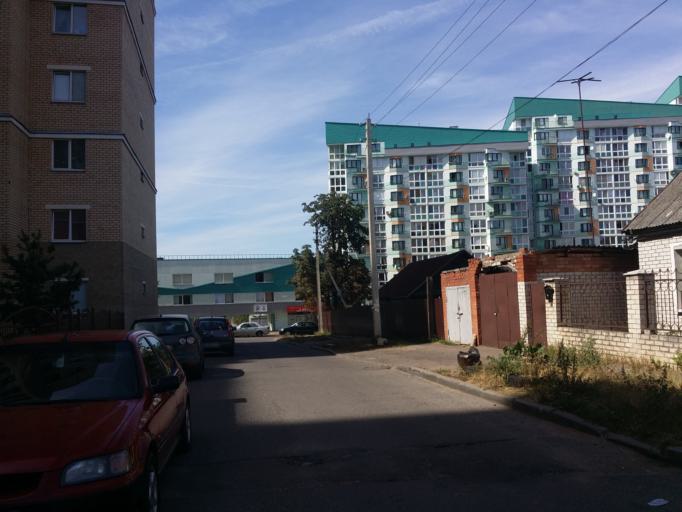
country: BY
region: Minsk
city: Minsk
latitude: 53.9416
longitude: 27.5984
